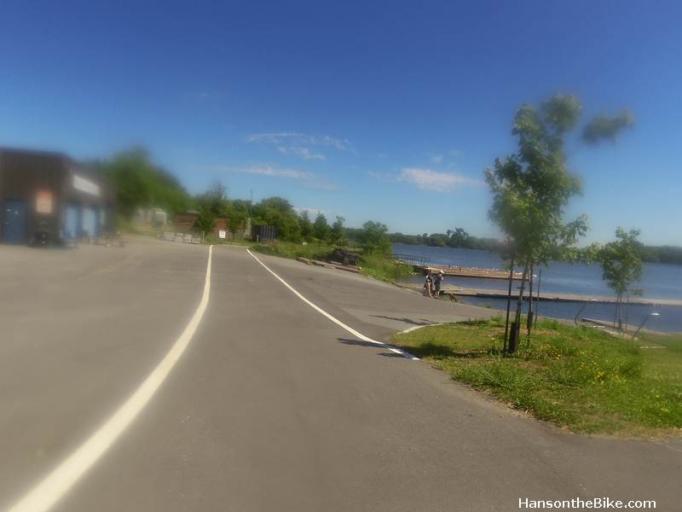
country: CA
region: Ontario
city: Kingston
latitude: 44.2428
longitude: -76.4800
